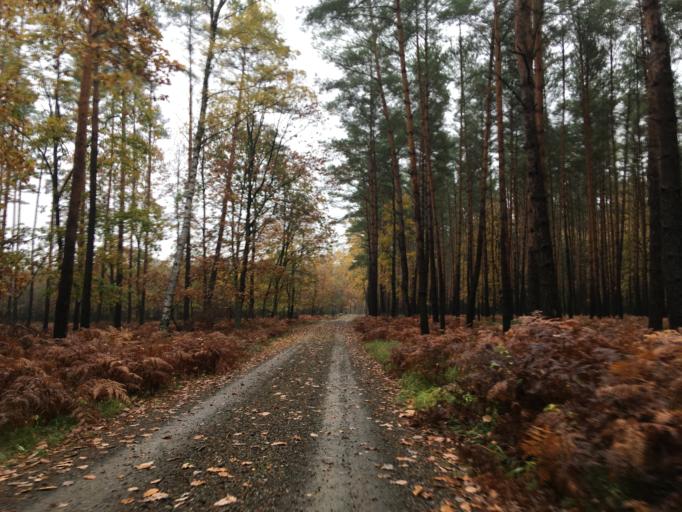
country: DE
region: Brandenburg
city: Beeskow
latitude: 52.2479
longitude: 14.2912
